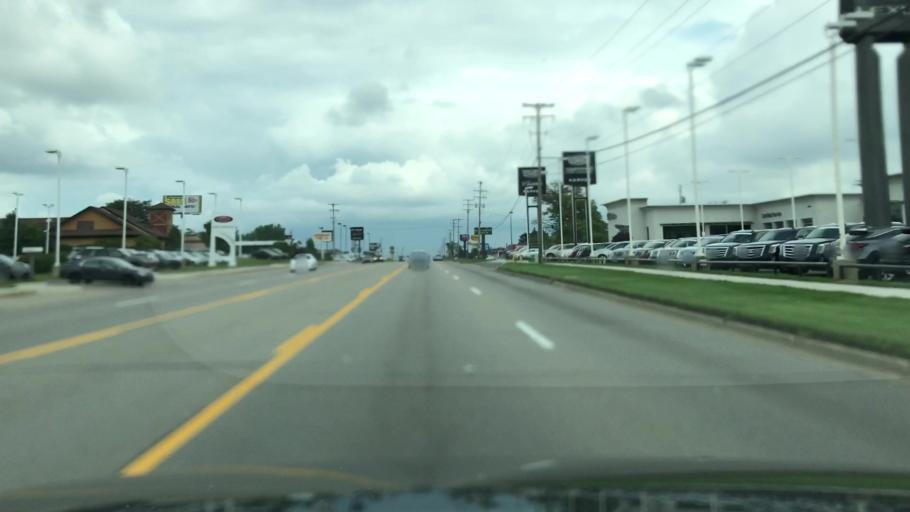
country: US
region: Michigan
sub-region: Kent County
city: East Grand Rapids
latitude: 42.9126
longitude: -85.6040
